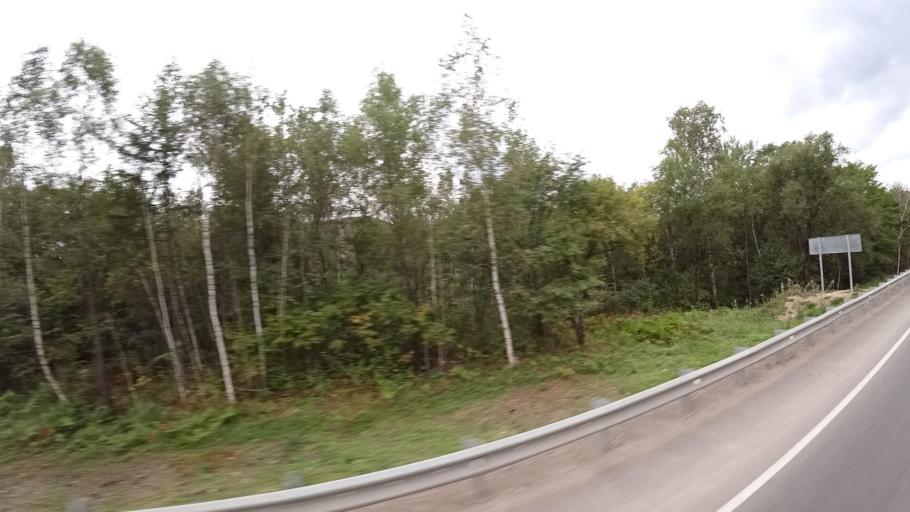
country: RU
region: Jewish Autonomous Oblast
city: Khingansk
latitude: 48.9855
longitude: 131.1403
